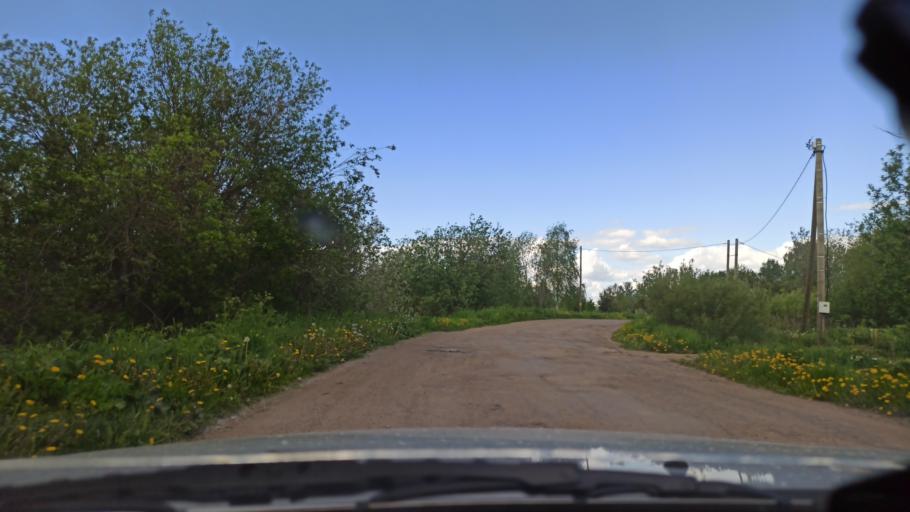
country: RU
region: Vologda
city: Vologda
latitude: 59.3288
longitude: 39.8362
